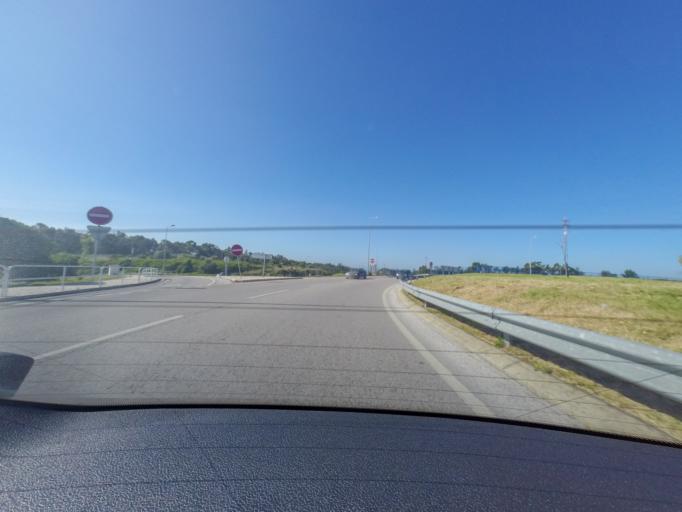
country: PT
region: Lisbon
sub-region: Cascais
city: Alcabideche
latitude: 38.7520
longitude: -9.3885
